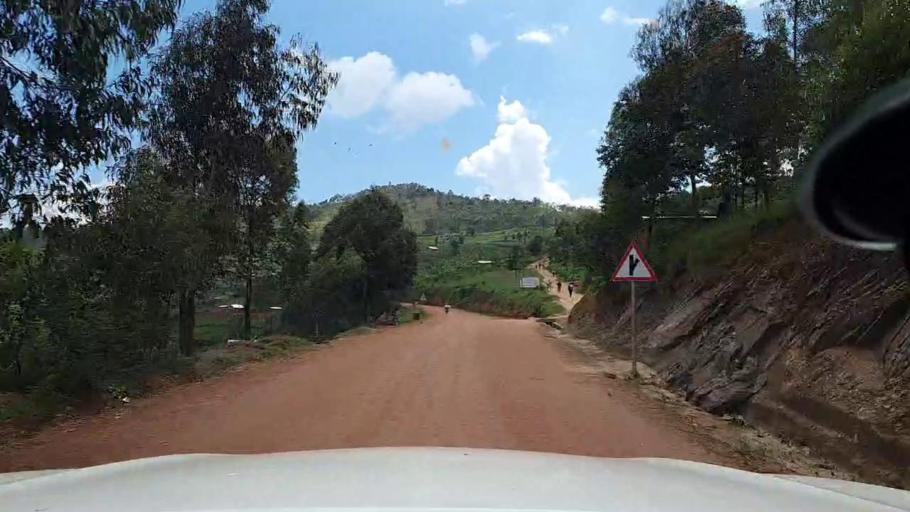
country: RW
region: Kigali
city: Kigali
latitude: -1.7770
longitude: 29.8407
